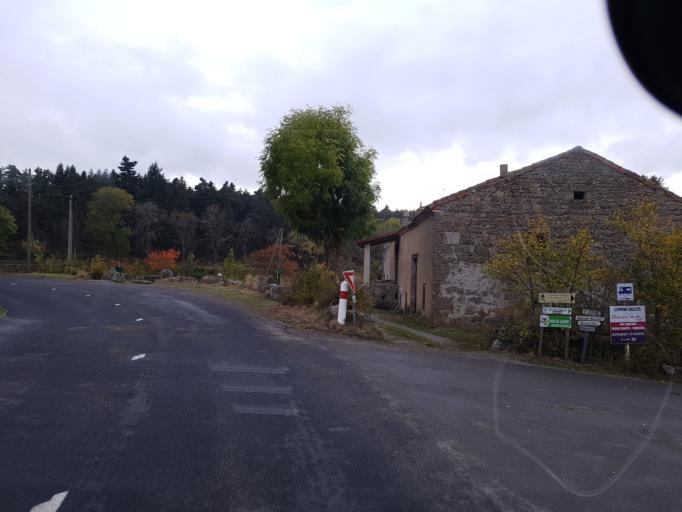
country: FR
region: Languedoc-Roussillon
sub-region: Departement de la Lozere
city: Langogne
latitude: 44.7211
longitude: 3.7810
